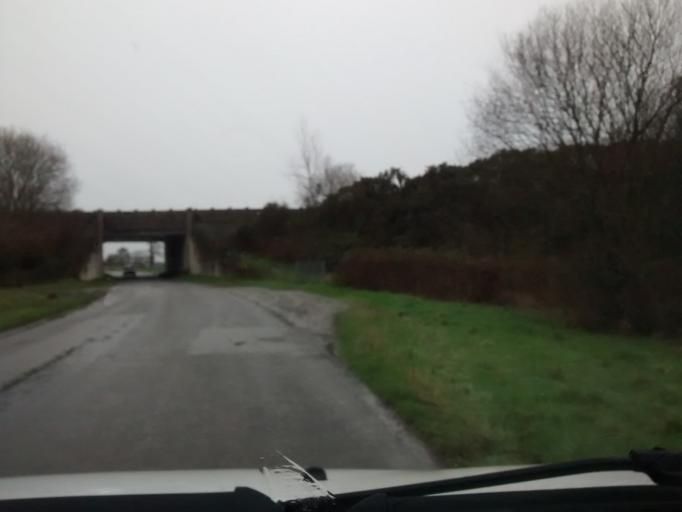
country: FR
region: Brittany
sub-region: Departement d'Ille-et-Vilaine
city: Gosne
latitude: 48.2420
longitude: -1.4586
